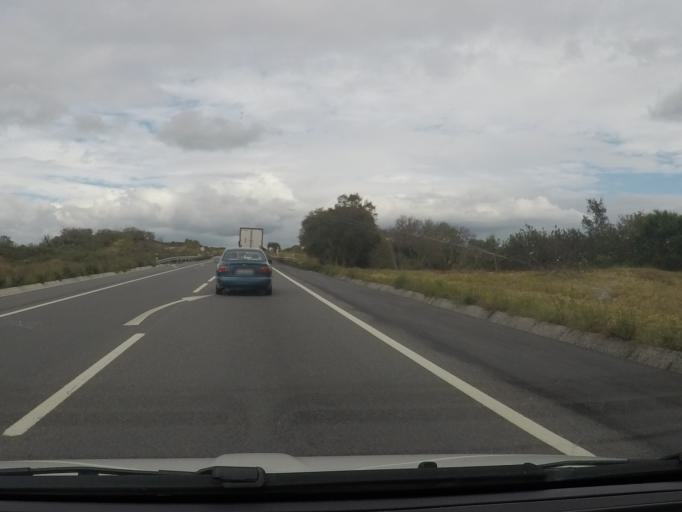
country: PT
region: Setubal
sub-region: Santiago do Cacem
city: Santiago do Cacem
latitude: 38.0682
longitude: -8.6861
